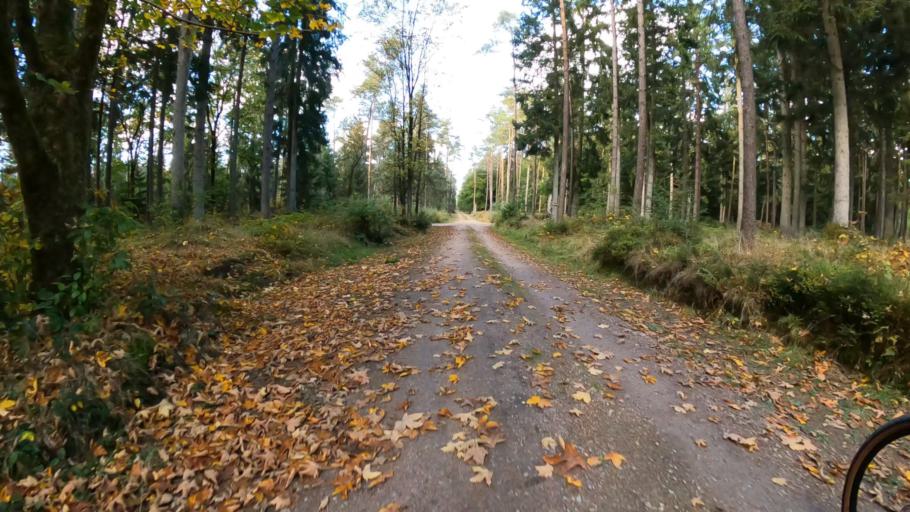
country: DE
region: Schleswig-Holstein
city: Hartenholm
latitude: 53.9310
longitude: 10.0769
